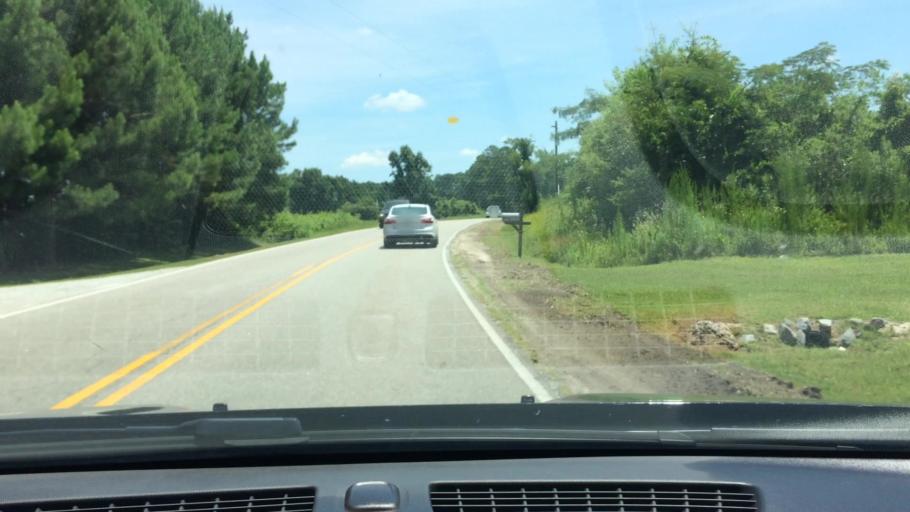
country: US
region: North Carolina
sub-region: Beaufort County
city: Washington
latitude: 35.5671
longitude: -77.2056
